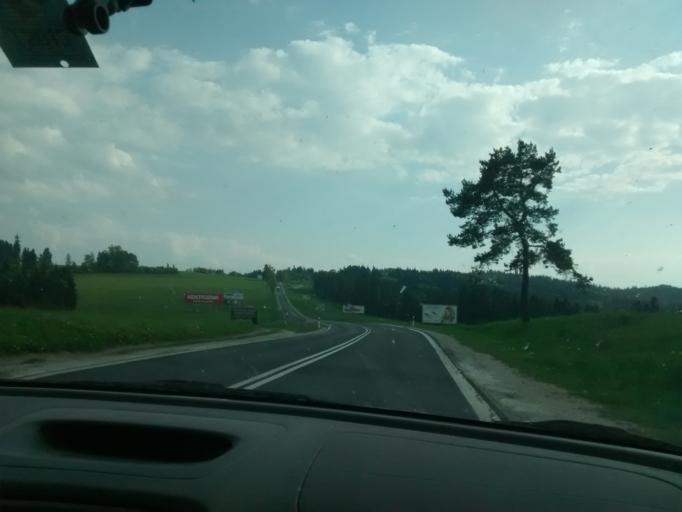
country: PL
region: Lesser Poland Voivodeship
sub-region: Powiat nowotarski
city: Rokiciny
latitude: 49.5695
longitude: 19.9464
